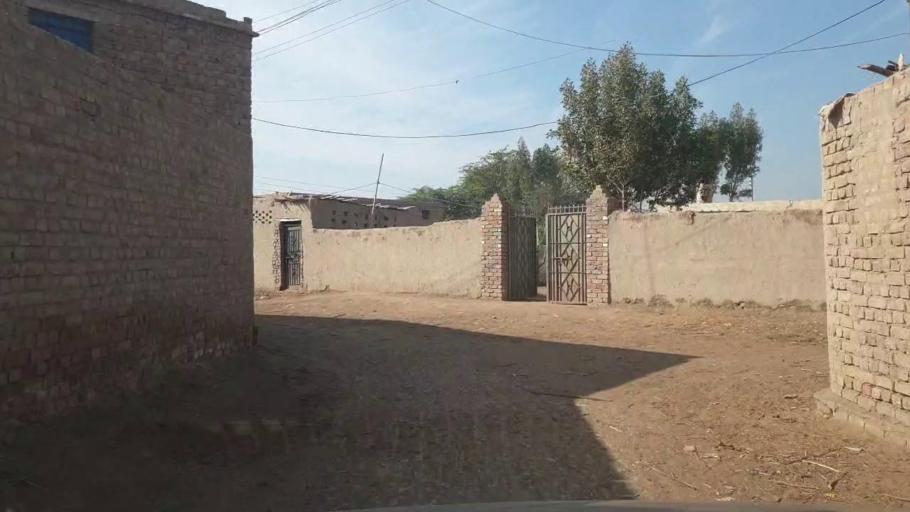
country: PK
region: Sindh
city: Shahpur Chakar
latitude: 26.1740
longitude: 68.5843
